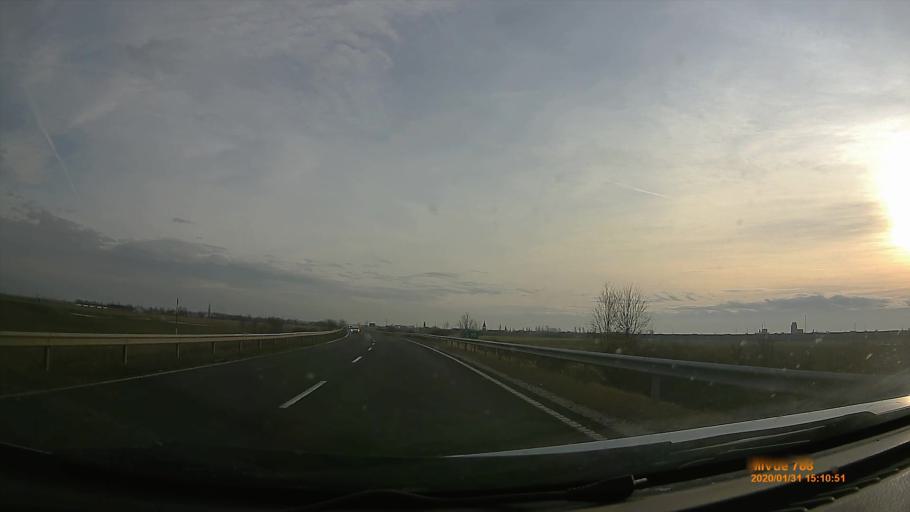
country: HU
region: Hajdu-Bihar
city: Polgar
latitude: 47.8563
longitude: 21.1503
